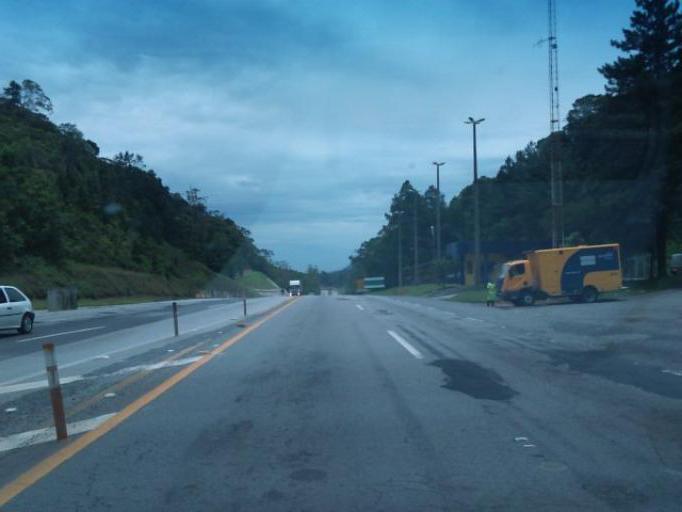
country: BR
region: Sao Paulo
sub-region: Juquitiba
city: Juquitiba
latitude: -24.0299
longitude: -47.1779
